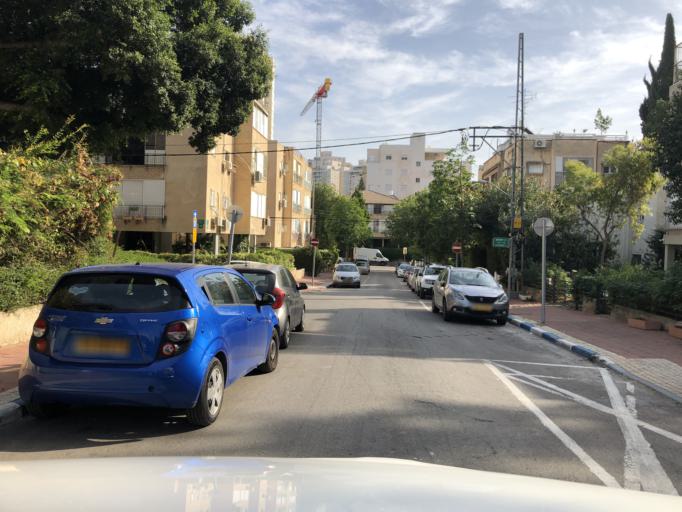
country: IL
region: Tel Aviv
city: Bene Beraq
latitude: 32.0709
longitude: 34.8260
